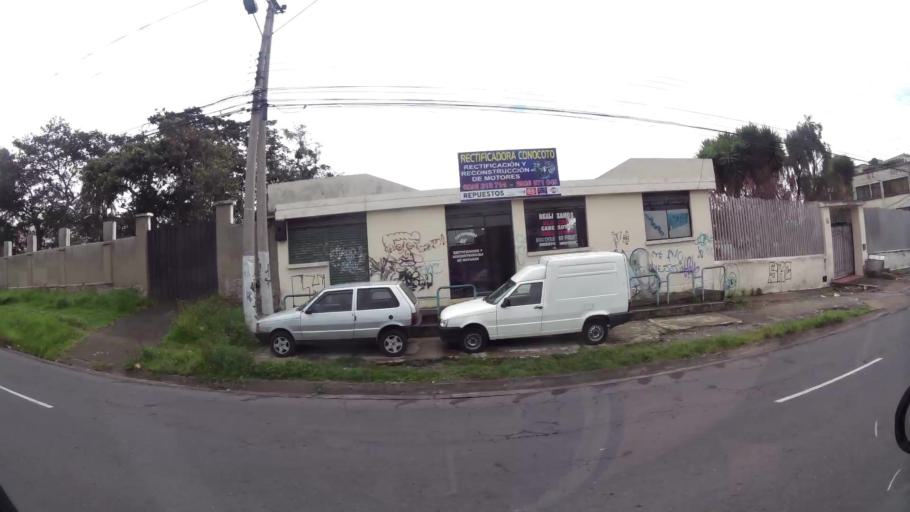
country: EC
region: Pichincha
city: Sangolqui
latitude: -0.3038
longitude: -78.4790
